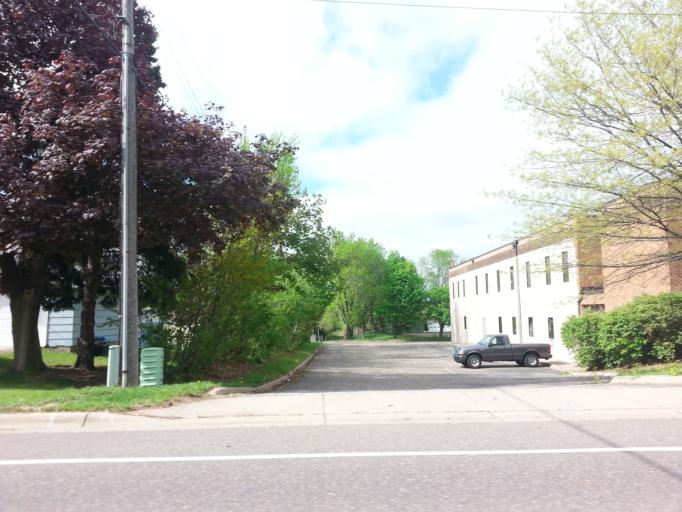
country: US
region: Minnesota
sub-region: Ramsey County
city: Maplewood
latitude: 44.9414
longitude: -92.9859
